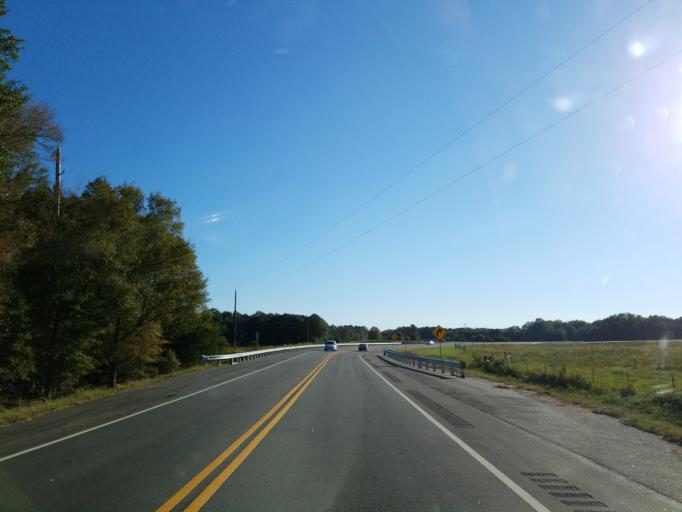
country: US
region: Georgia
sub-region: Lee County
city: Leesburg
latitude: 31.7520
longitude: -84.1560
